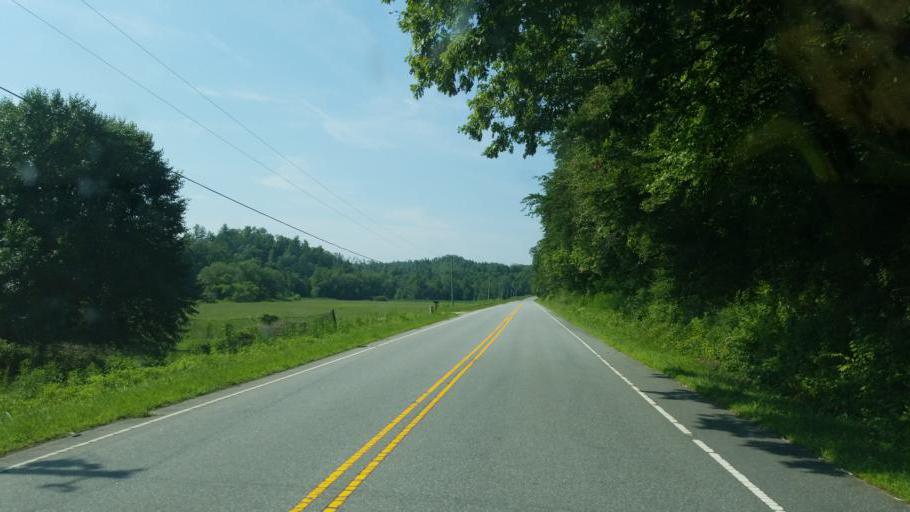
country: US
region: North Carolina
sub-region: Burke County
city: Glen Alpine
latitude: 35.8425
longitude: -81.7762
